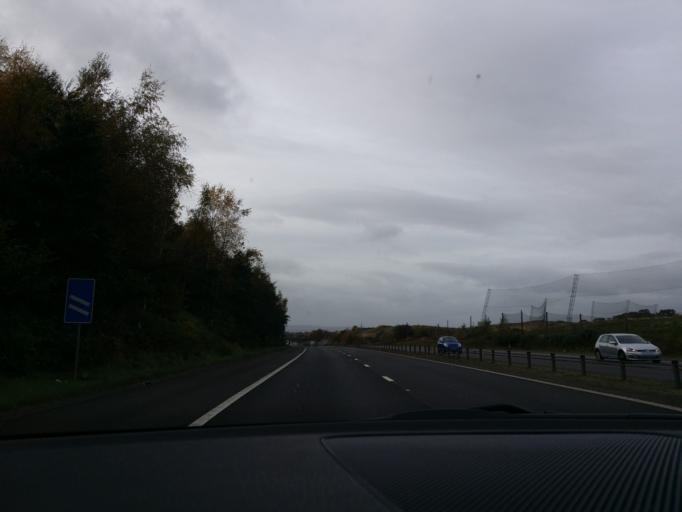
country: GB
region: Scotland
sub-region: Falkirk
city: Polmont
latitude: 55.9878
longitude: -3.6712
